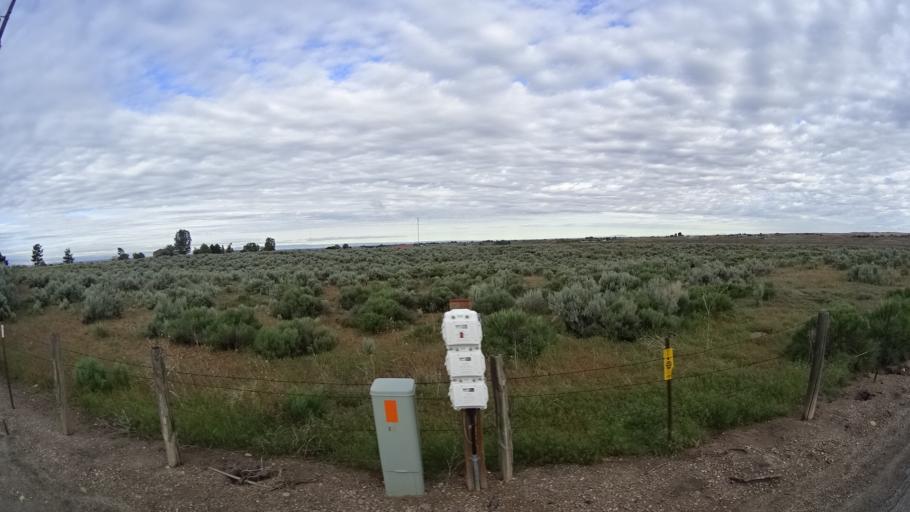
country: US
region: Idaho
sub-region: Ada County
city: Star
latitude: 43.7236
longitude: -116.5127
